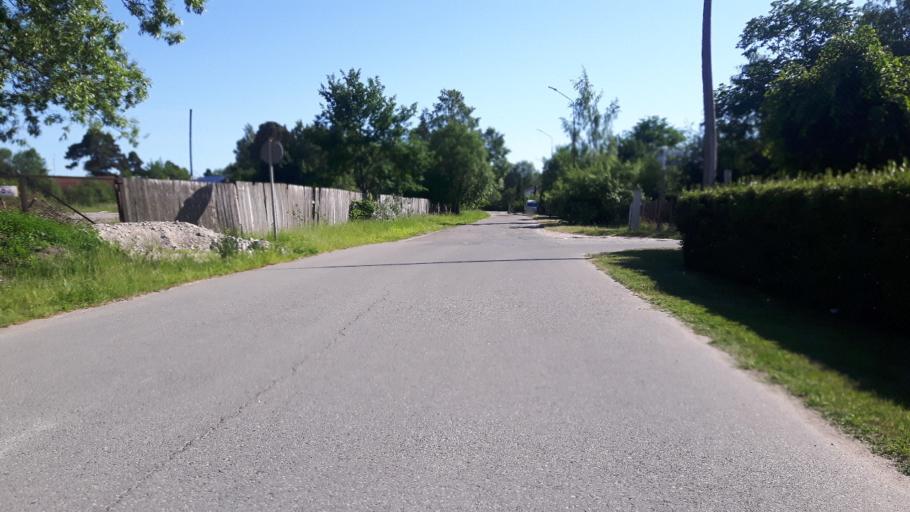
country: LV
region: Salacgrivas
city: Salacgriva
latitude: 57.7491
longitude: 24.3547
